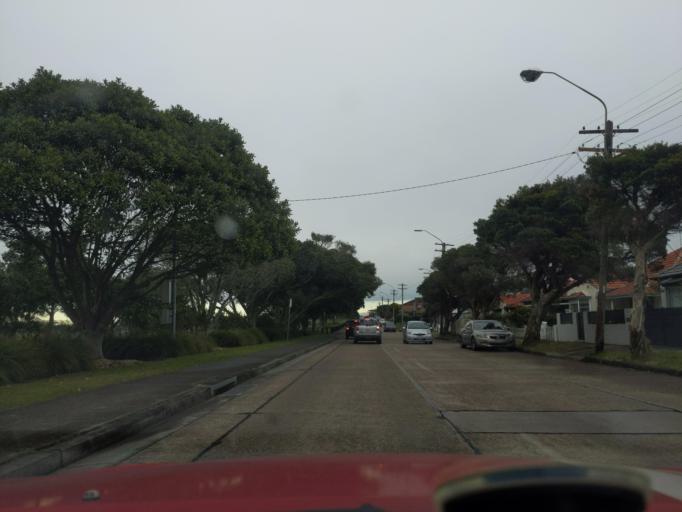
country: AU
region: New South Wales
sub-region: Randwick
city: Maroubra
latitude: -33.9465
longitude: 151.2375
